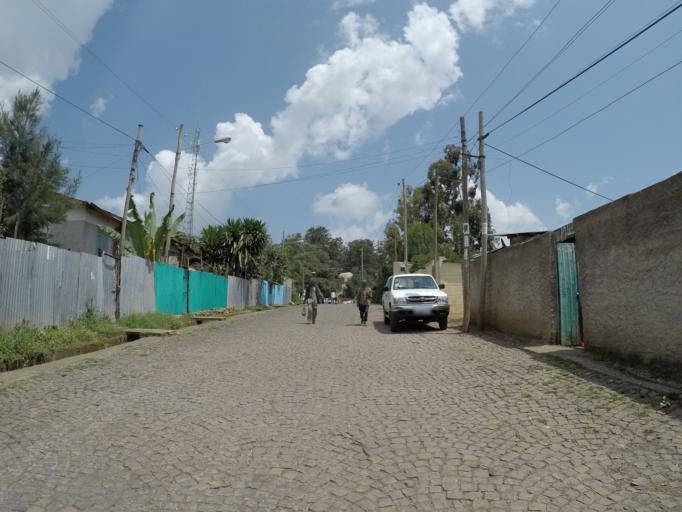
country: ET
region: Amhara
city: Gondar
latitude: 12.6133
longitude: 37.4791
